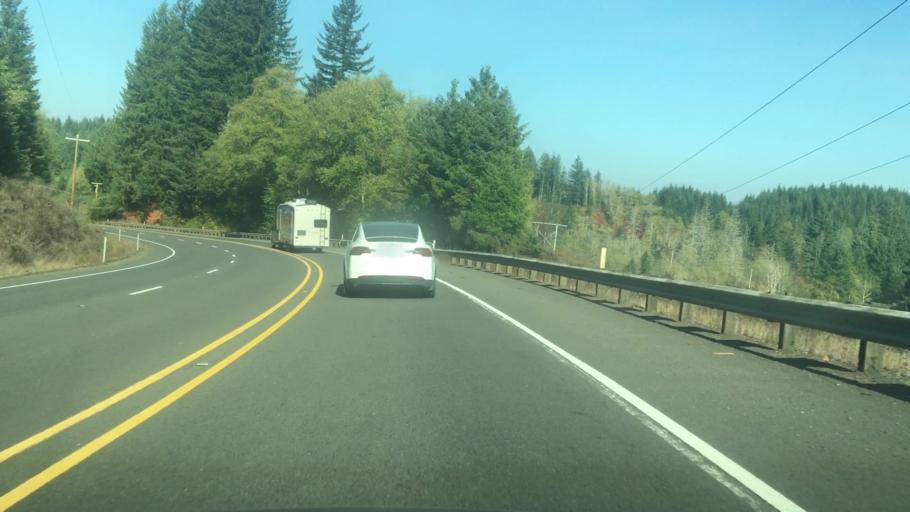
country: US
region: Oregon
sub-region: Polk County
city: Grand Ronde
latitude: 45.0645
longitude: -123.7291
